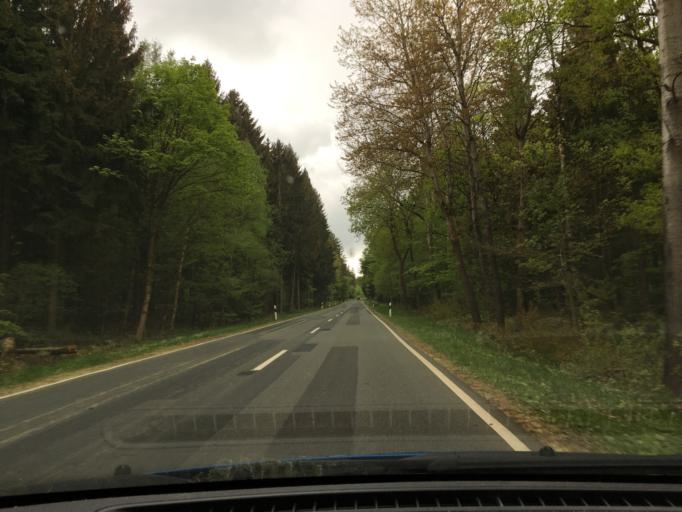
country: DE
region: Lower Saxony
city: Heinade
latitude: 51.7961
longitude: 9.6322
